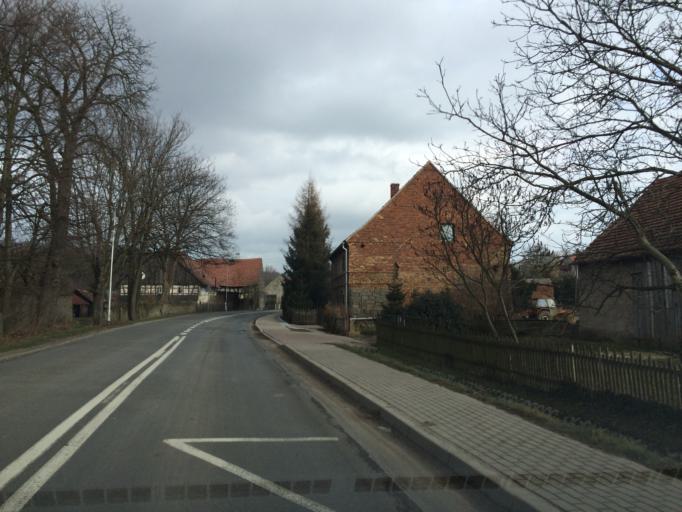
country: PL
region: Lower Silesian Voivodeship
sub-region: Powiat lwowecki
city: Lwowek Slaski
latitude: 51.1121
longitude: 15.6040
